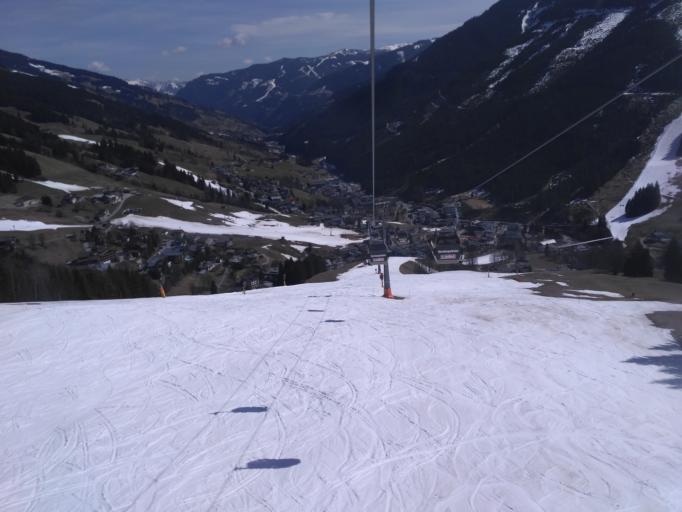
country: AT
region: Salzburg
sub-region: Politischer Bezirk Zell am See
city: Saalbach
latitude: 47.3977
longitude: 12.6274
